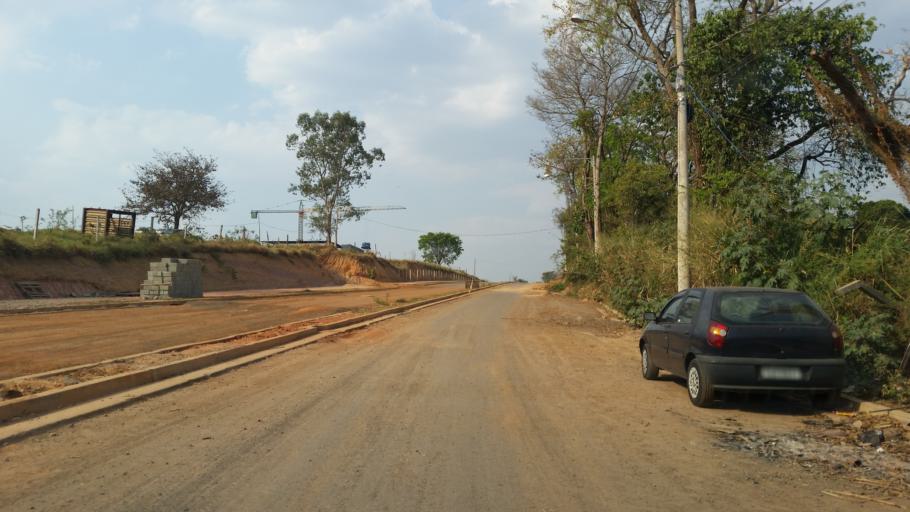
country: BR
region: Sao Paulo
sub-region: Hortolandia
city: Hortolandia
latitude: -22.8817
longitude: -47.1845
